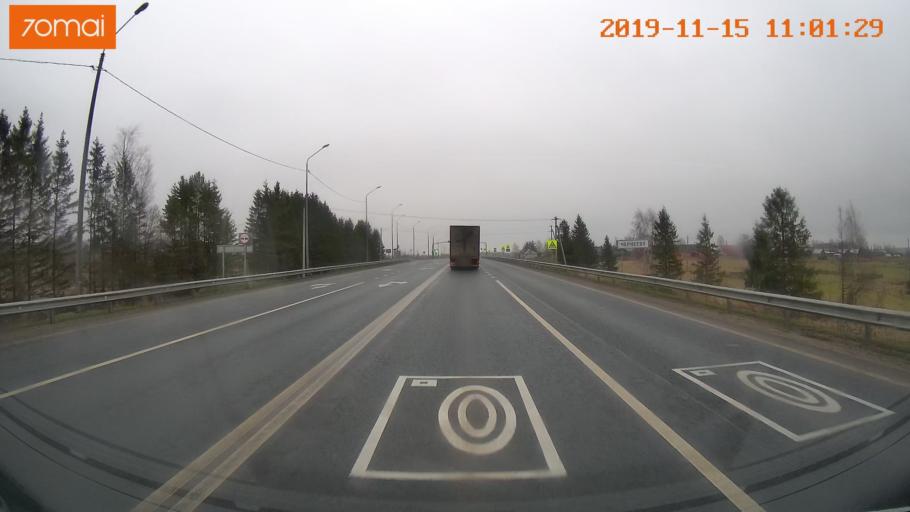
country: RU
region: Vologda
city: Chebsara
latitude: 59.1326
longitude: 38.9219
